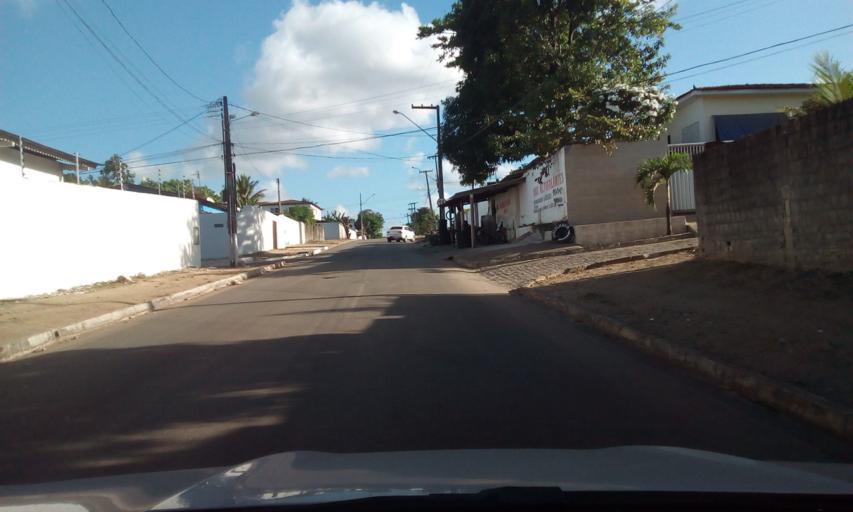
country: BR
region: Paraiba
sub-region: Bayeux
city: Bayeux
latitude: -7.1382
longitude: -34.9098
